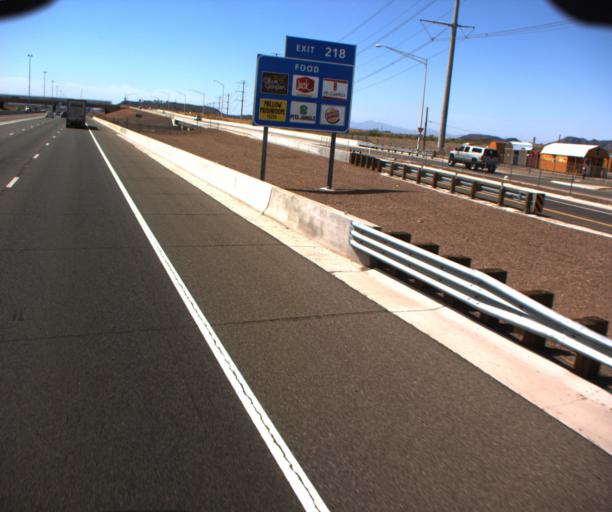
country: US
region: Arizona
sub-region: Maricopa County
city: Anthem
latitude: 33.7301
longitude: -112.1213
